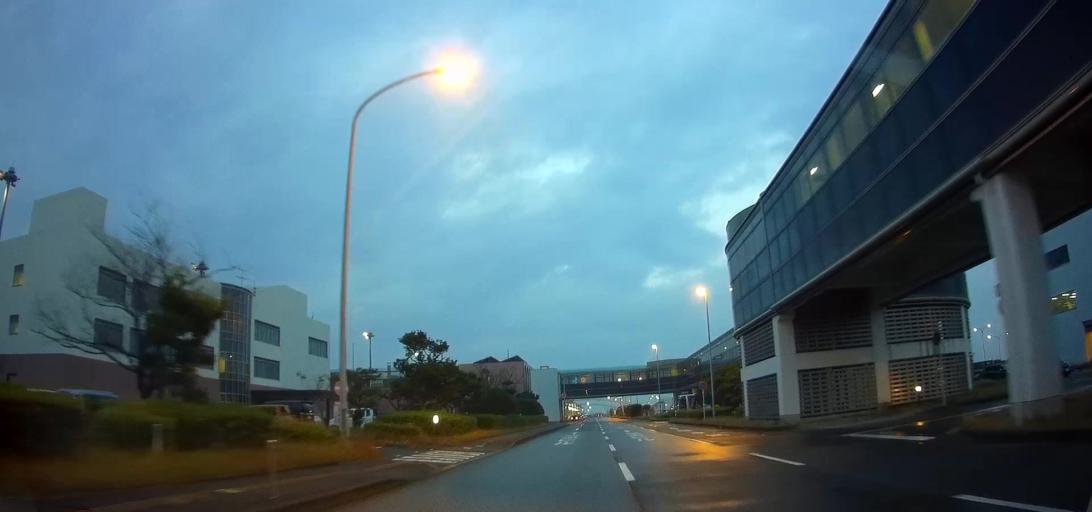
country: JP
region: Nagasaki
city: Omura
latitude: 32.9126
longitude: 129.9246
